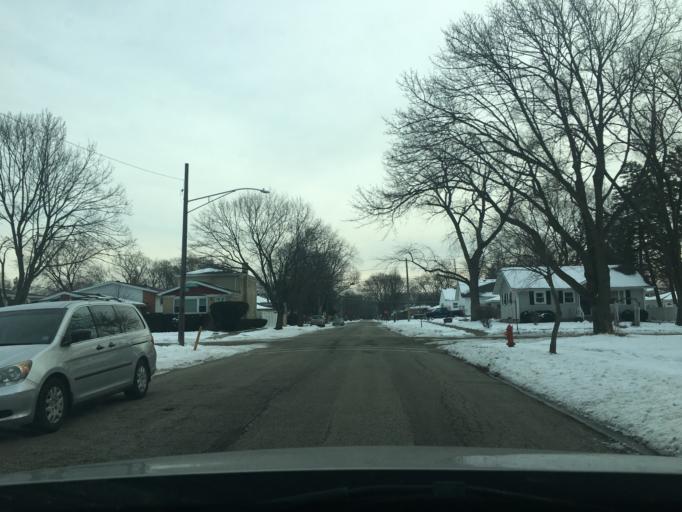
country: US
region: Illinois
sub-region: Cook County
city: Des Plaines
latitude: 42.0207
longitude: -87.8812
